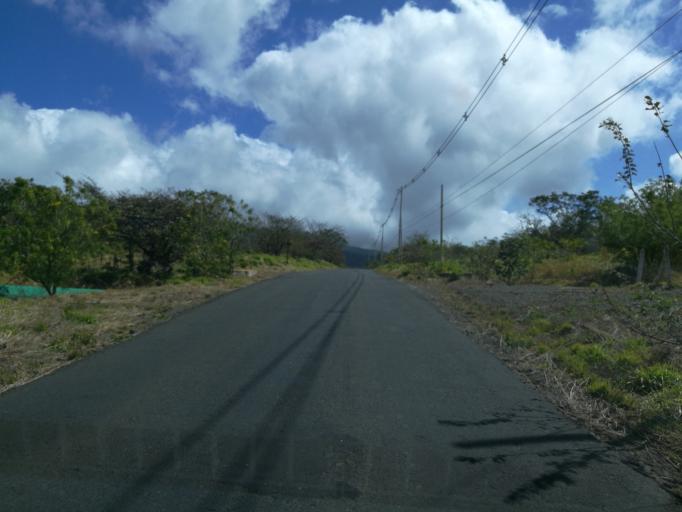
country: CR
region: Guanacaste
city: Liberia
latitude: 10.7612
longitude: -85.3575
